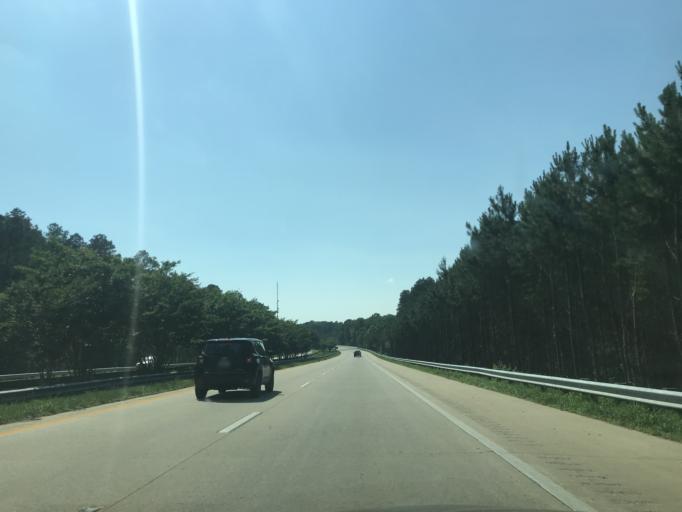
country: US
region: Maryland
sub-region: Wicomico County
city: Salisbury
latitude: 38.4037
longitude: -75.5885
